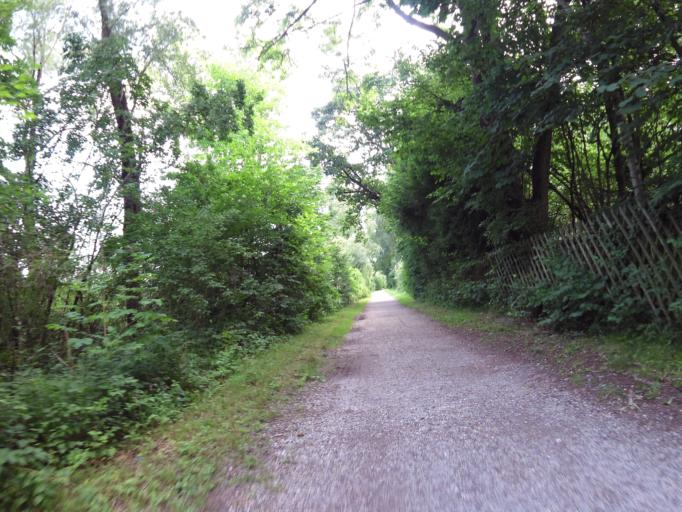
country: DE
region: Bavaria
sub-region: Upper Bavaria
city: Andechs
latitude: 47.9806
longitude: 11.1552
